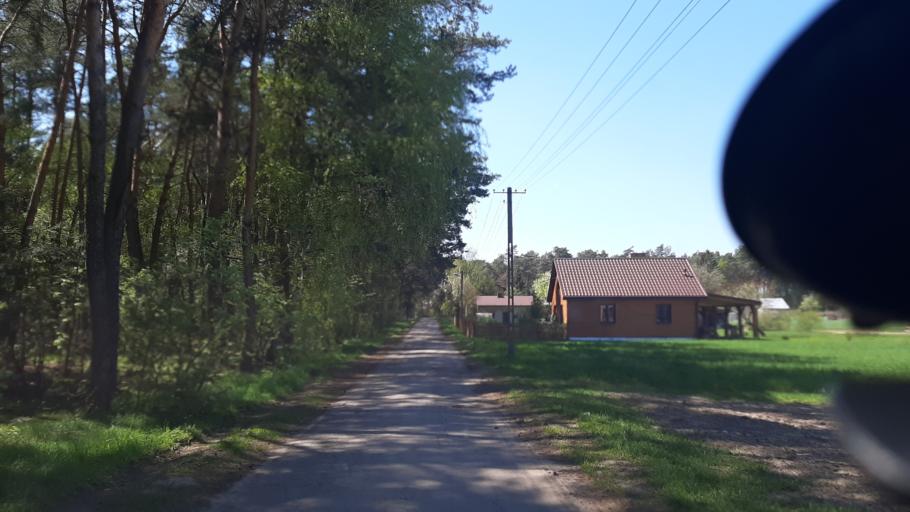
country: PL
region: Lublin Voivodeship
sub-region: Powiat lubartowski
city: Abramow
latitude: 51.4264
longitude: 22.2811
